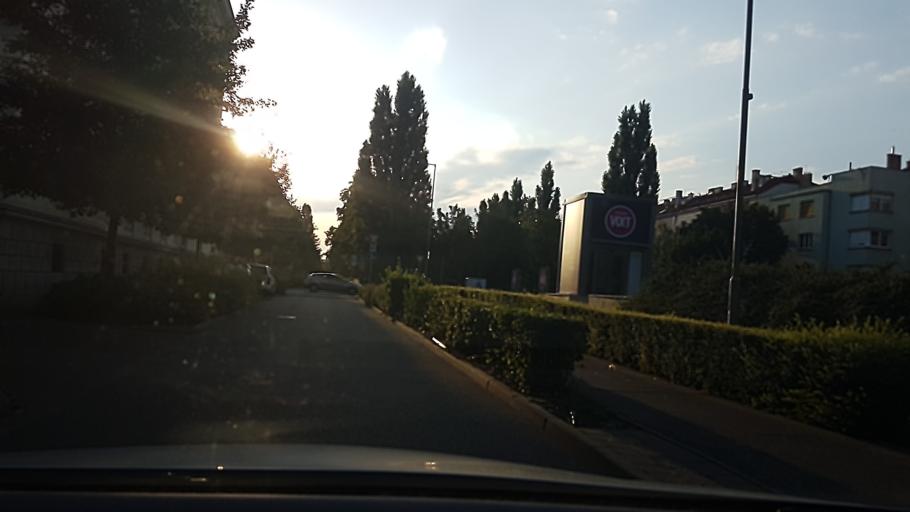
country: HU
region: Gyor-Moson-Sopron
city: Sopron
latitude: 47.6797
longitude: 16.5893
